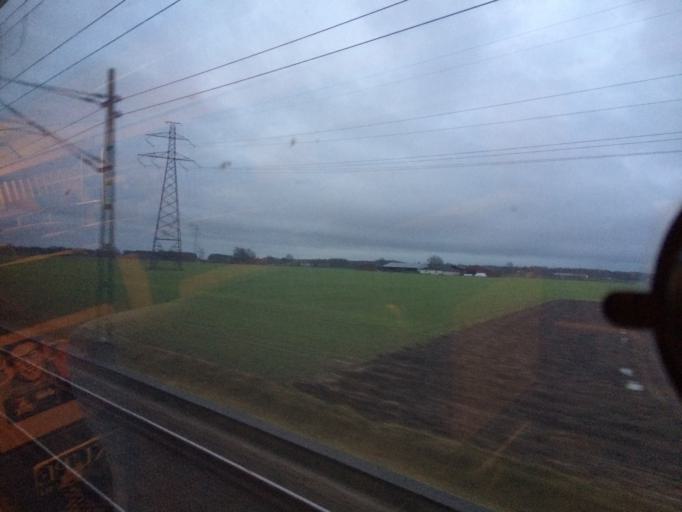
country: SE
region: Skane
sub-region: Kavlinge Kommun
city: Hofterup
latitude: 55.8325
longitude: 12.9879
